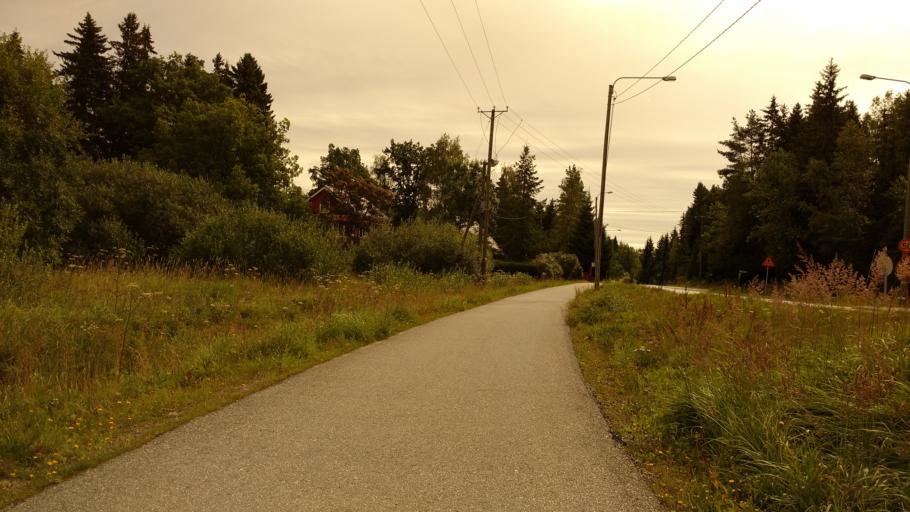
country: FI
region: Varsinais-Suomi
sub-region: Turku
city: Kaarina
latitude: 60.4462
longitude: 22.4176
